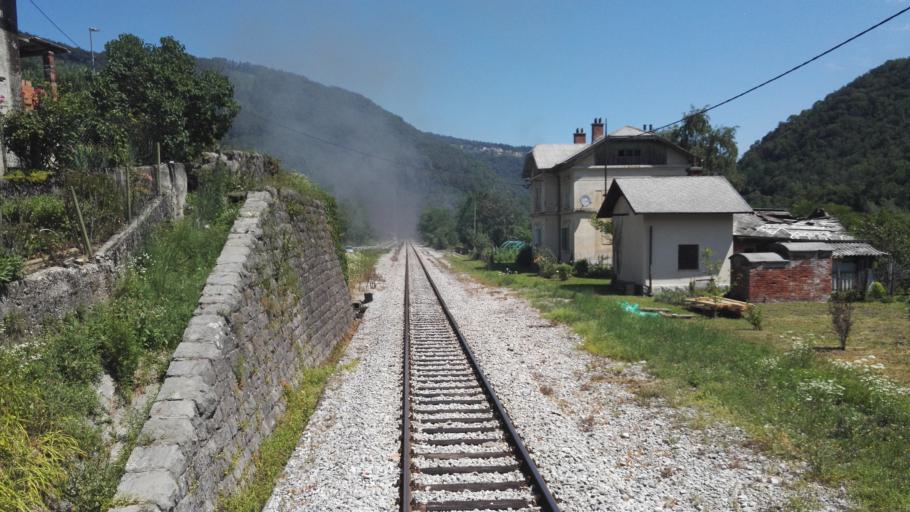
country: SI
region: Kanal
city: Deskle
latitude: 46.0428
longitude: 13.5881
